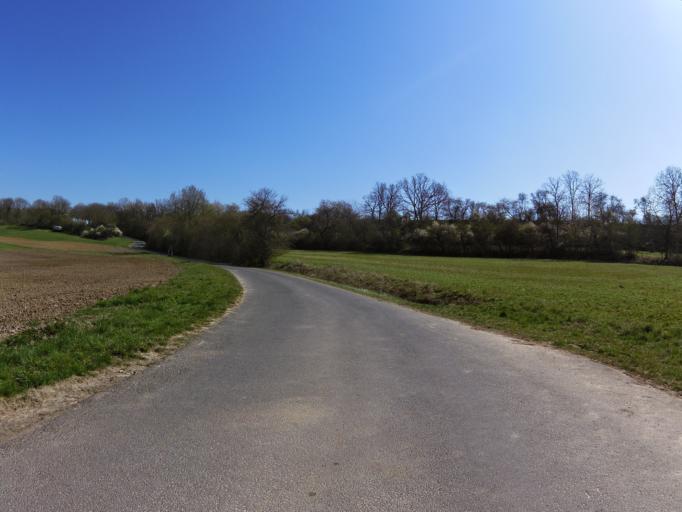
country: DE
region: Bavaria
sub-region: Regierungsbezirk Unterfranken
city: Kurnach
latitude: 49.8404
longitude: 10.0563
